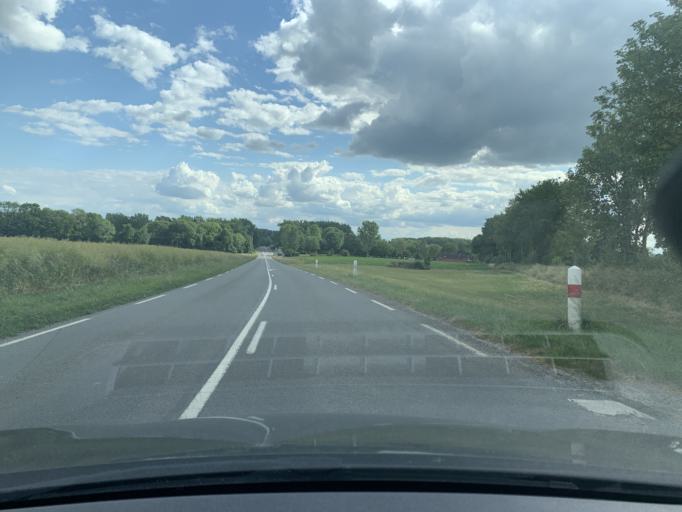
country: FR
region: Picardie
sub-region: Departement de la Somme
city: Peronne
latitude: 49.9411
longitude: 2.9497
